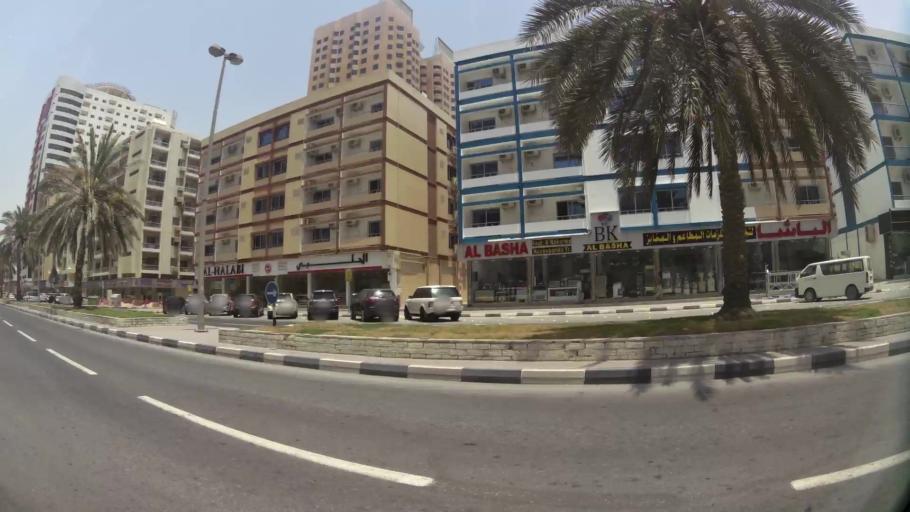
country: AE
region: Ash Shariqah
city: Sharjah
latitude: 25.3167
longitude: 55.3820
